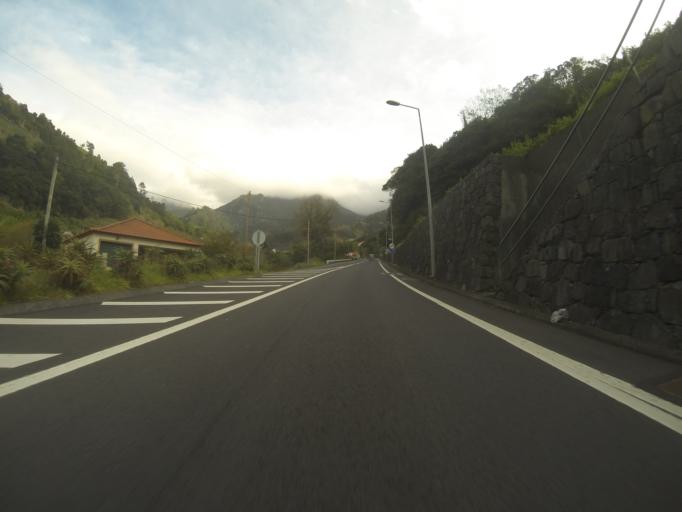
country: PT
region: Madeira
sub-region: Sao Vicente
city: Sao Vicente
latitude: 32.7799
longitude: -17.0331
